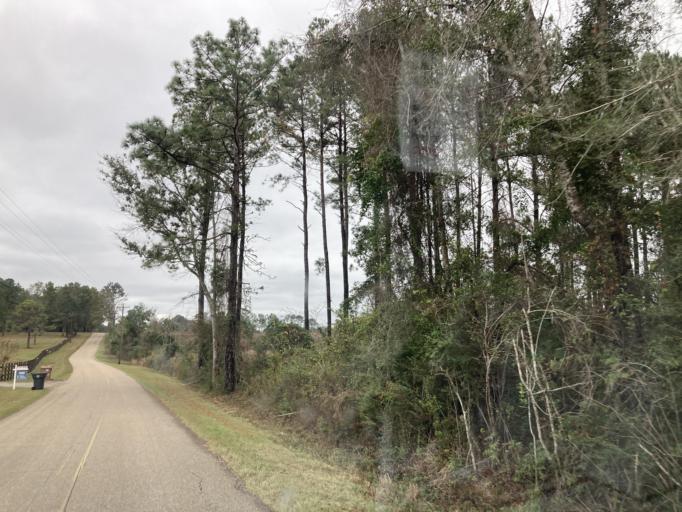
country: US
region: Mississippi
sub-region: Lamar County
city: West Hattiesburg
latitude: 31.2668
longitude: -89.5059
